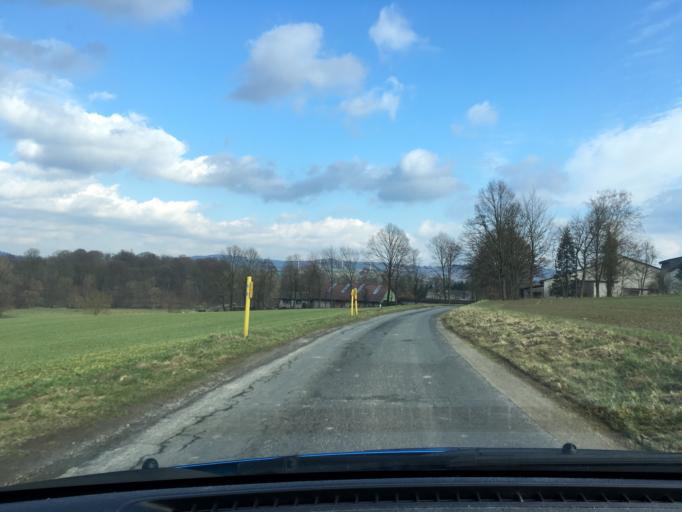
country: DE
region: Lower Saxony
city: Uslar
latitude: 51.6442
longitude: 9.6305
